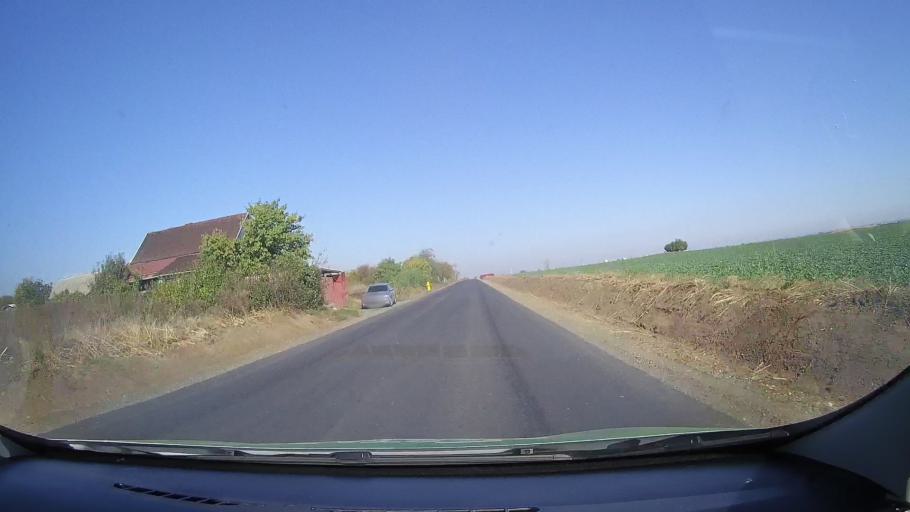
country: RO
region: Satu Mare
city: Carei
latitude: 47.6575
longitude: 22.4603
